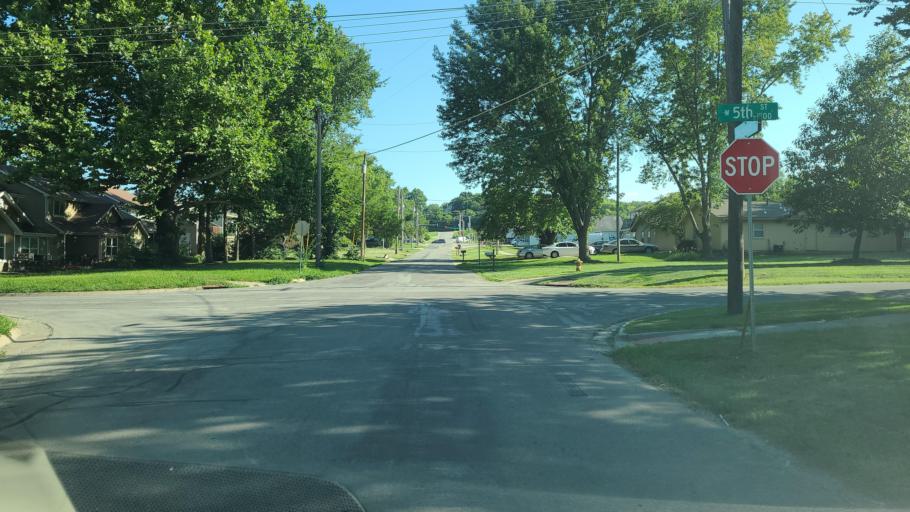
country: US
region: Kansas
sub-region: Douglas County
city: Lawrence
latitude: 38.9753
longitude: -95.2545
